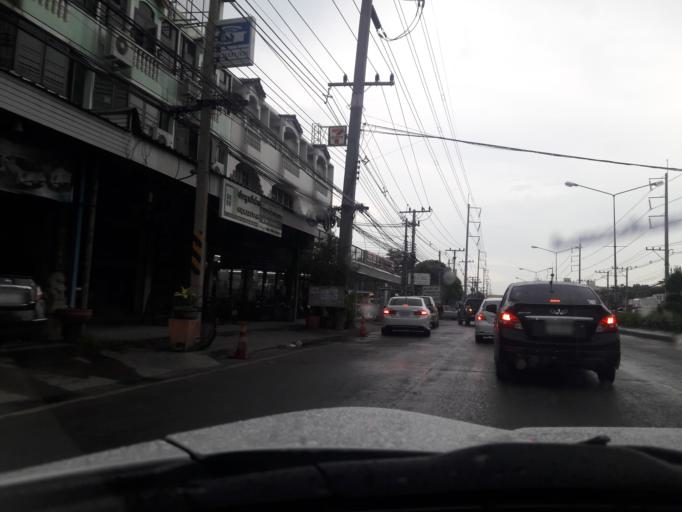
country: TH
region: Lop Buri
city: Lop Buri
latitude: 14.7905
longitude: 100.6739
